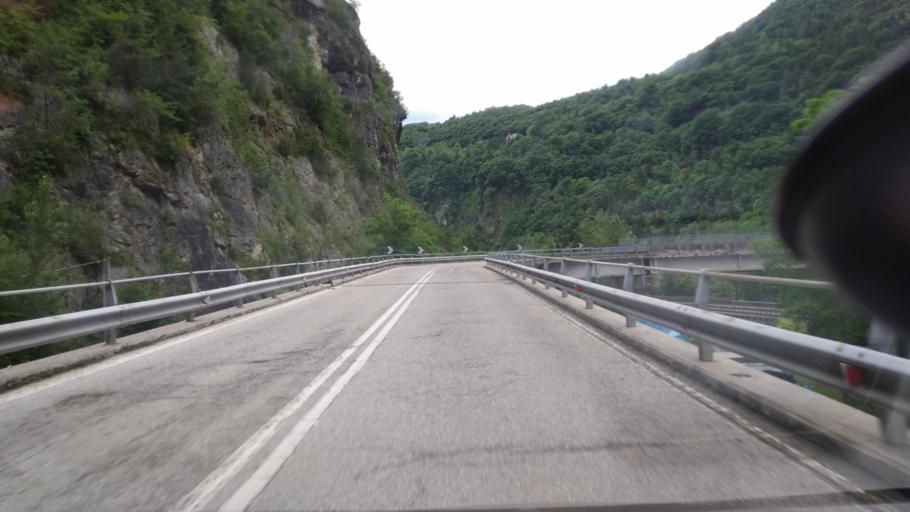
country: IT
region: Veneto
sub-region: Provincia di Vicenza
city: Enego
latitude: 45.9587
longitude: 11.7103
